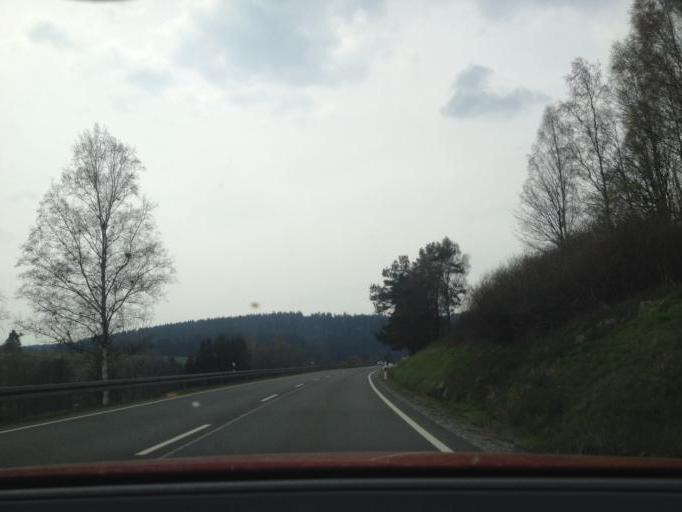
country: DE
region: Bavaria
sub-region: Upper Franconia
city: Bischofsgrun
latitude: 50.0575
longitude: 11.7958
